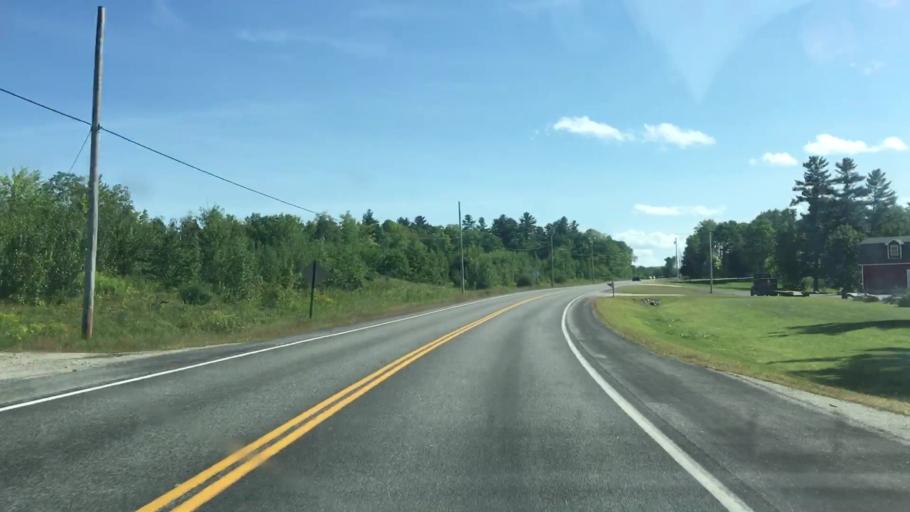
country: US
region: Maine
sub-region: Androscoggin County
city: Lisbon
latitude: 44.0477
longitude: -70.0775
